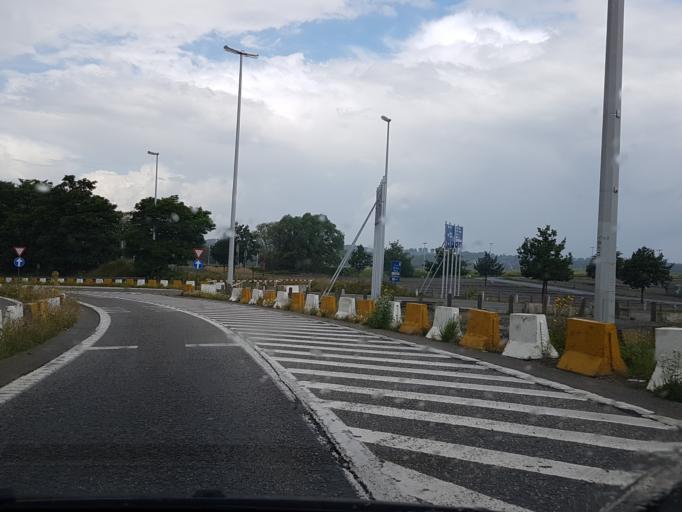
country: BE
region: Flanders
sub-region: Provincie Vlaams-Brabant
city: Bever
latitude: 50.9014
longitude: 4.3306
